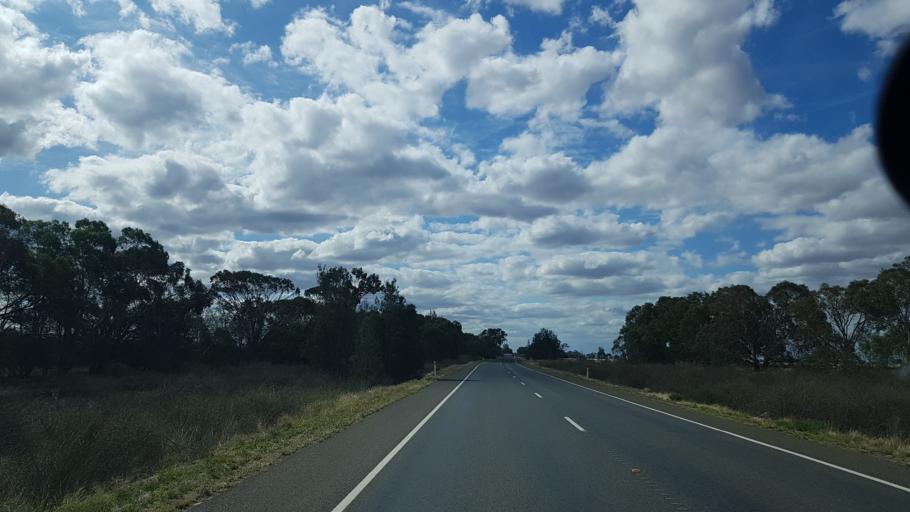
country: AU
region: Victoria
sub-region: Swan Hill
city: Swan Hill
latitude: -35.9888
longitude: 143.9461
